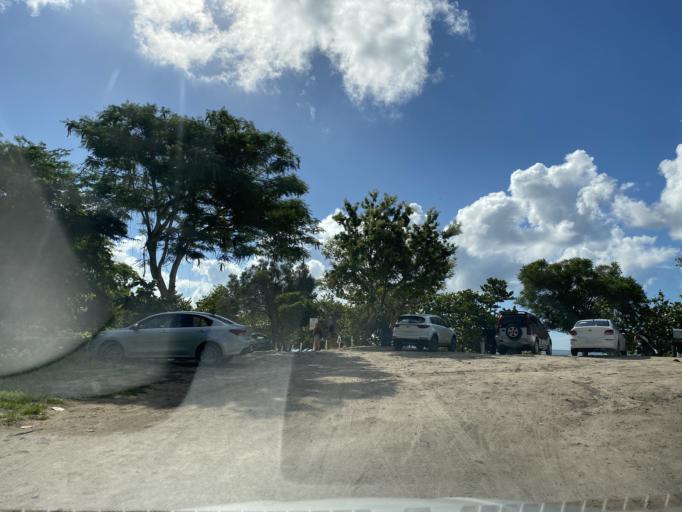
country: DO
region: La Romana
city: La Romana
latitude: 18.3644
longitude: -68.8411
